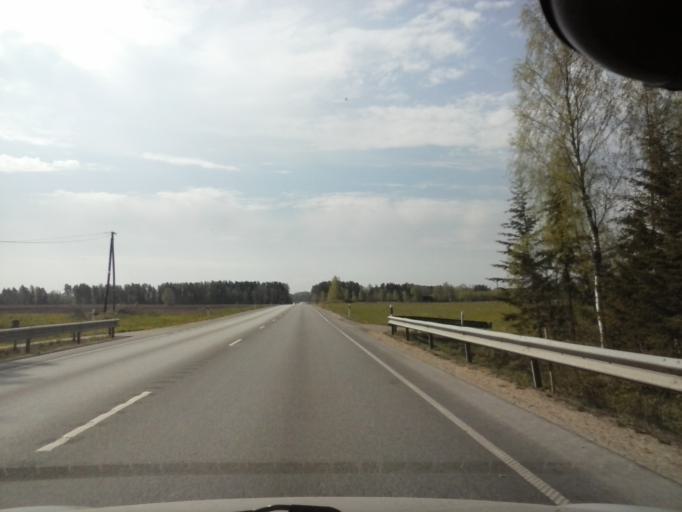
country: EE
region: Tartu
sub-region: UElenurme vald
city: Ulenurme
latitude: 58.2213
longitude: 26.7020
